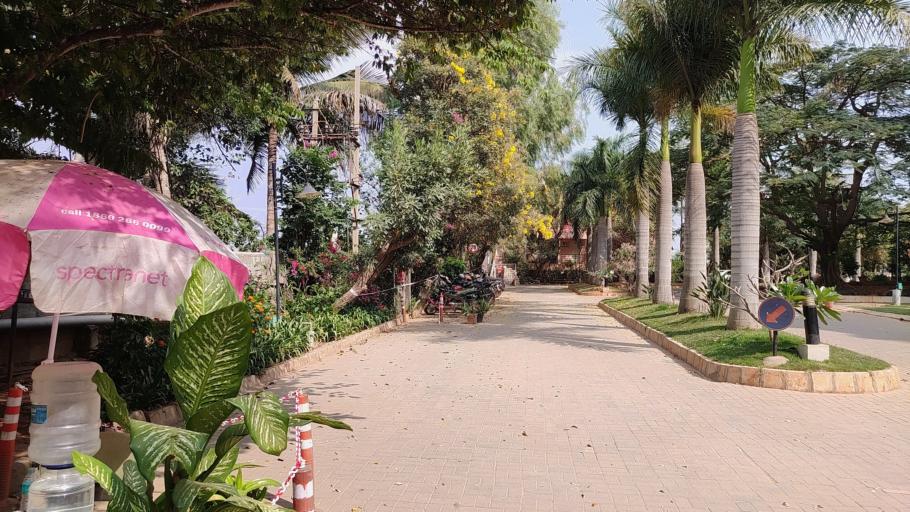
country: IN
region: Karnataka
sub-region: Bangalore Urban
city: Bangalore
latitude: 12.9525
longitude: 77.7208
